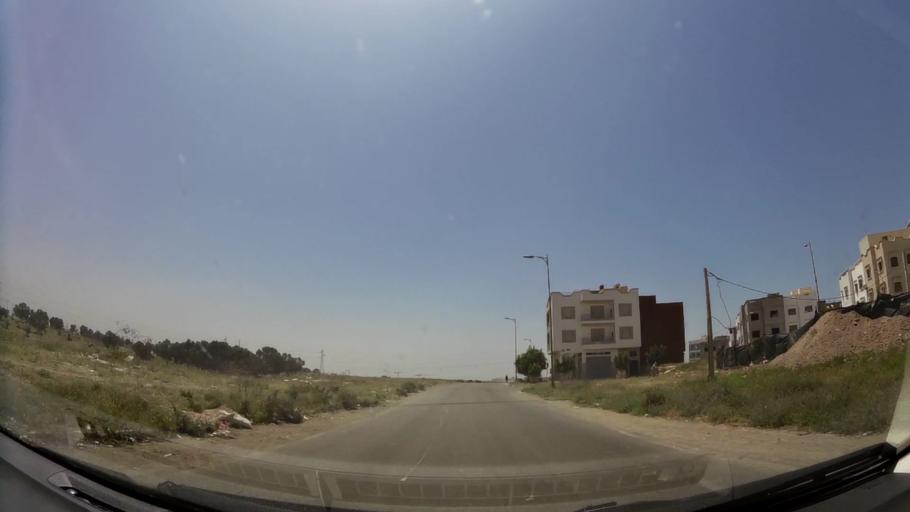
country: MA
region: Oued ed Dahab-Lagouira
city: Dakhla
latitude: 30.4271
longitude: -9.5523
